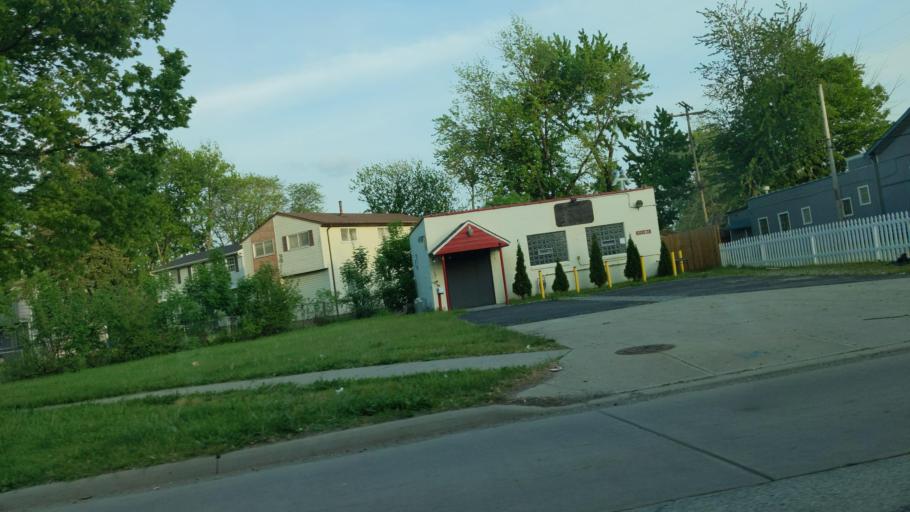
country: US
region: Ohio
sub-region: Cuyahoga County
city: Brooklyn
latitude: 41.4401
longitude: -81.7762
